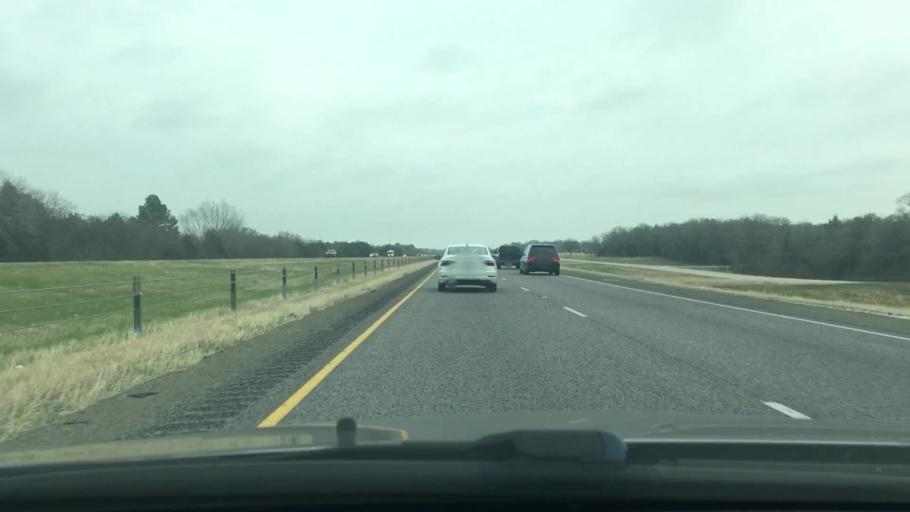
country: US
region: Texas
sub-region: Freestone County
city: Fairfield
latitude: 31.7453
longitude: -96.1951
